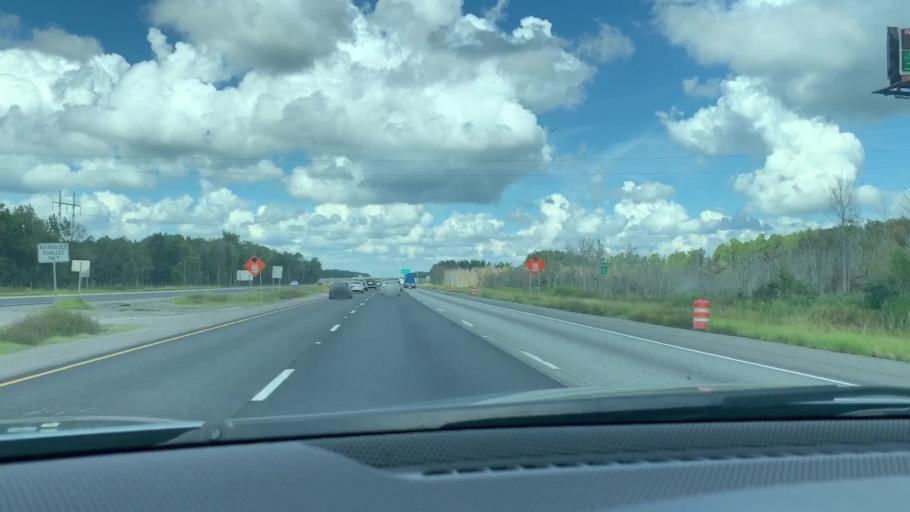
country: US
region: Georgia
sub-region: Camden County
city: Kingsland
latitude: 30.8160
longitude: -81.6643
